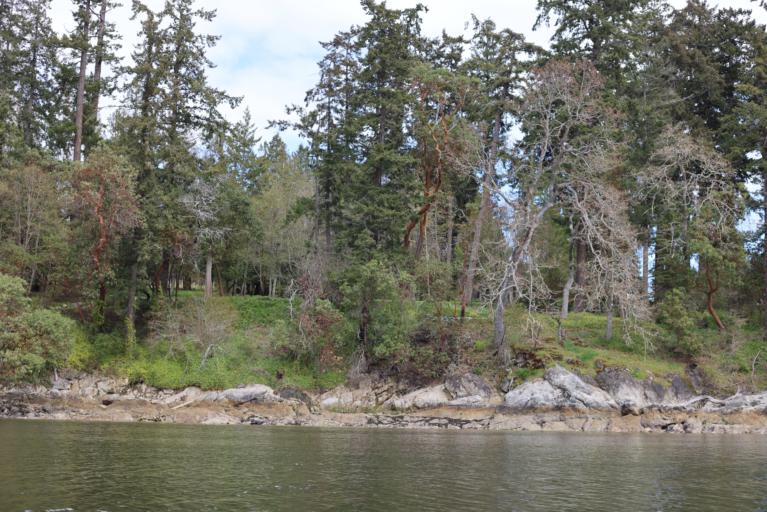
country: CA
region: British Columbia
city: North Saanich
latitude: 48.5915
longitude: -123.4690
